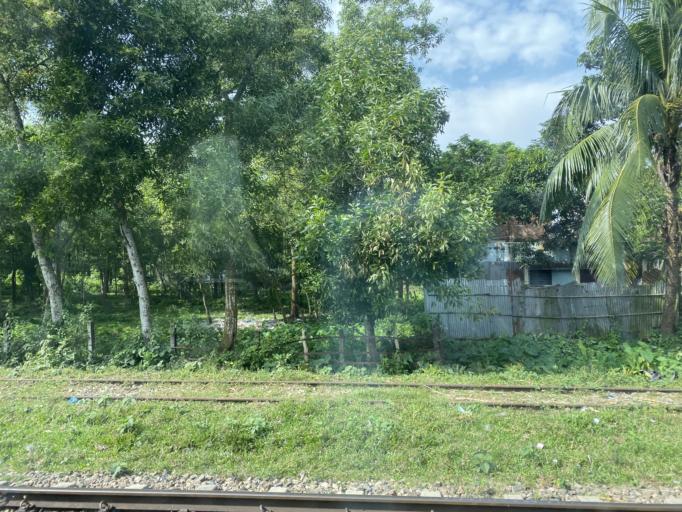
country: BD
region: Sylhet
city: Habiganj
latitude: 24.1783
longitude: 91.3572
